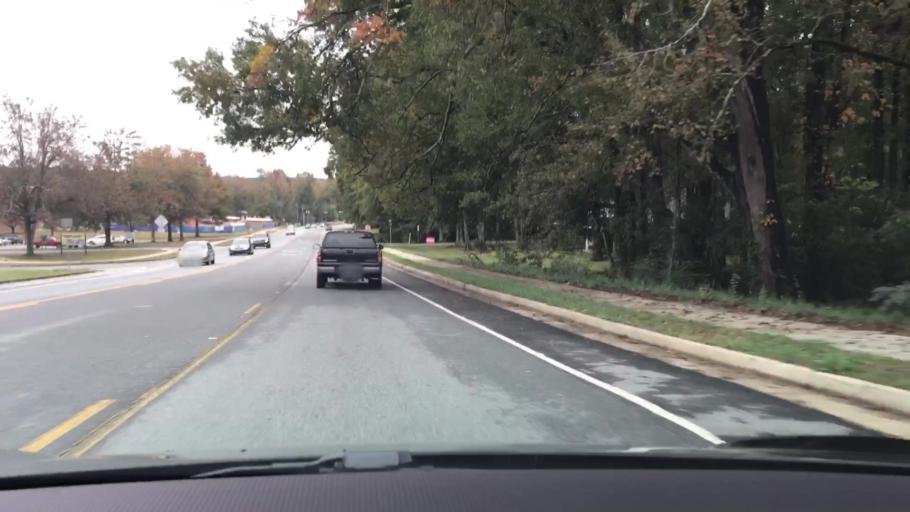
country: US
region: Georgia
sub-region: Greene County
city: Greensboro
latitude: 33.5656
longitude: -83.1838
